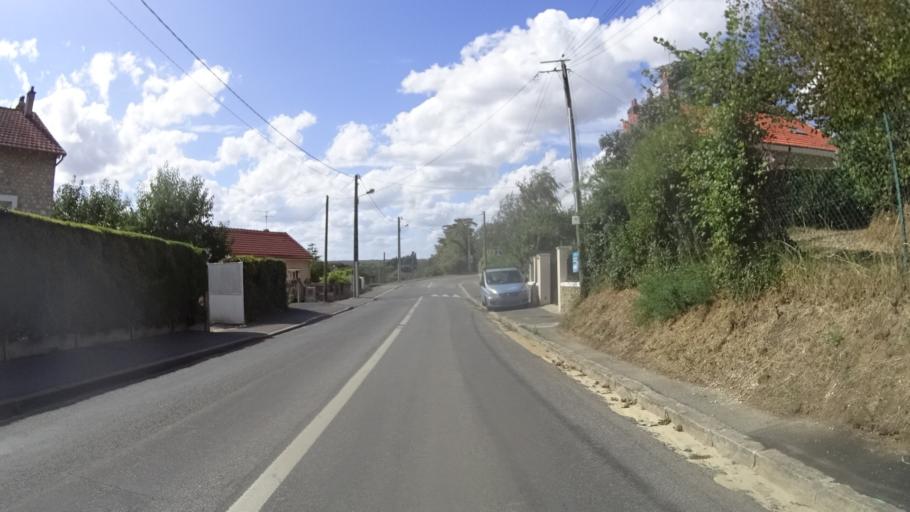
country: FR
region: Ile-de-France
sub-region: Departement de l'Essonne
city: La Ferte-Alais
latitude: 48.4790
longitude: 2.3529
